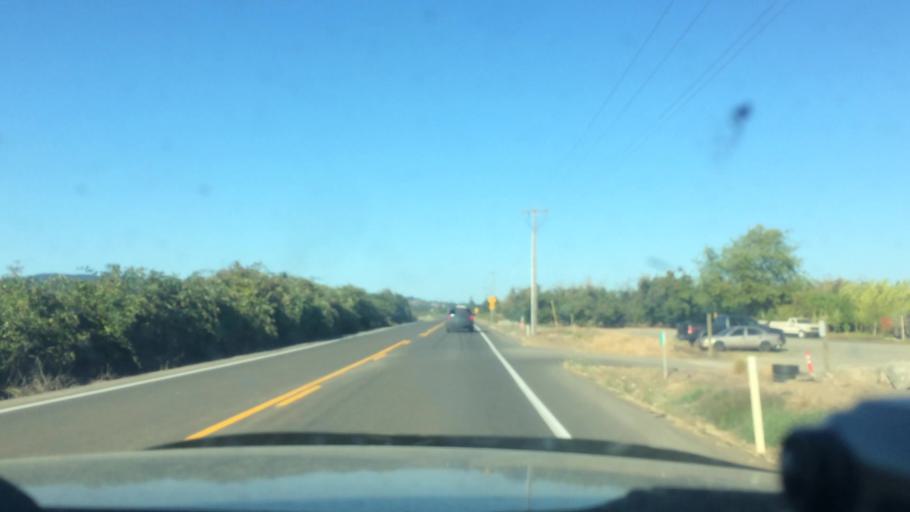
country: US
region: Oregon
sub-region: Yamhill County
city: Newberg
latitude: 45.2431
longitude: -122.9482
